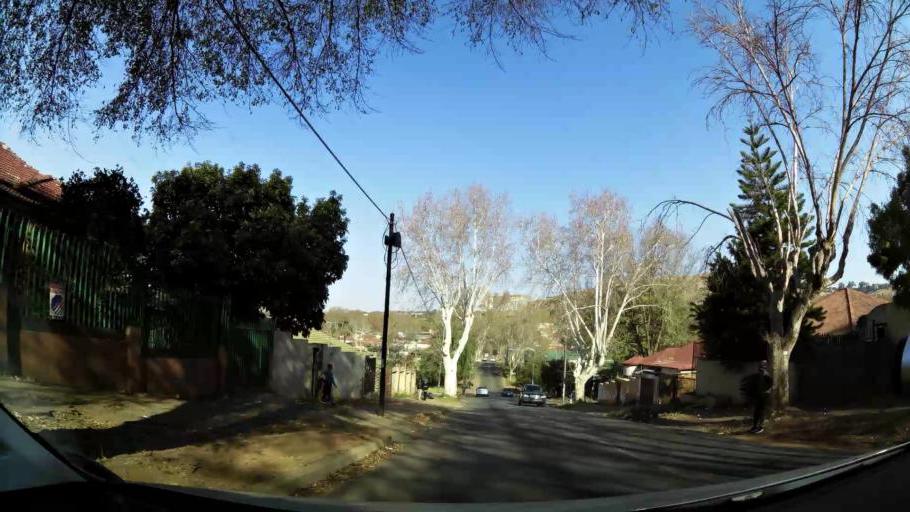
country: ZA
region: Gauteng
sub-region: City of Johannesburg Metropolitan Municipality
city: Johannesburg
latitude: -26.1871
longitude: 28.0853
